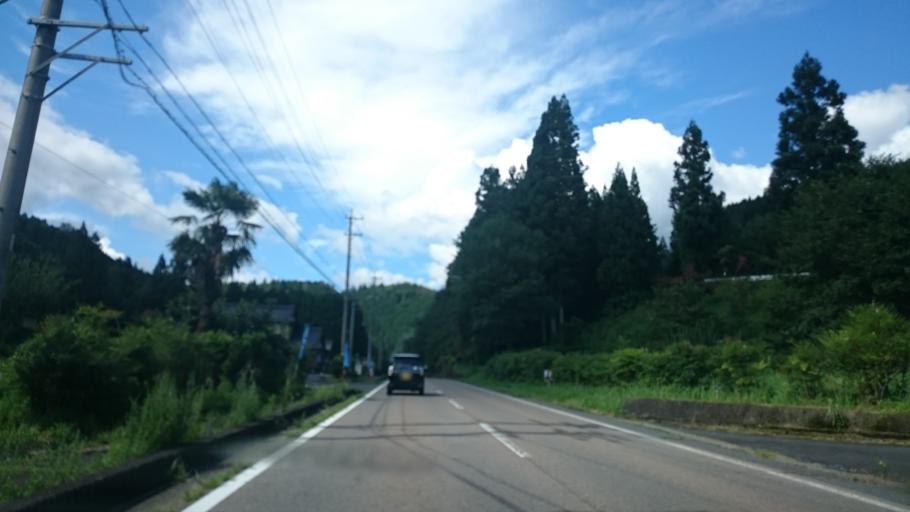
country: JP
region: Gifu
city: Nakatsugawa
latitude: 35.6034
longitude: 137.4638
